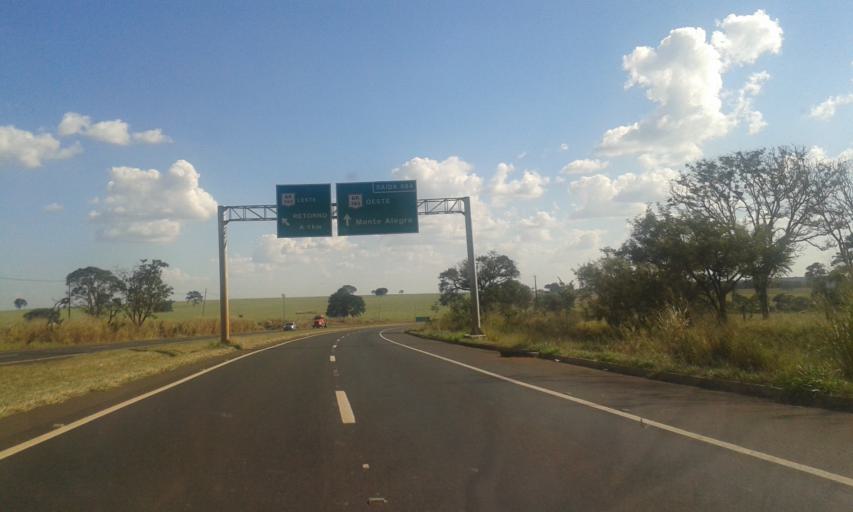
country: BR
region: Minas Gerais
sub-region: Monte Alegre De Minas
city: Monte Alegre de Minas
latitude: -18.8851
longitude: -48.6113
